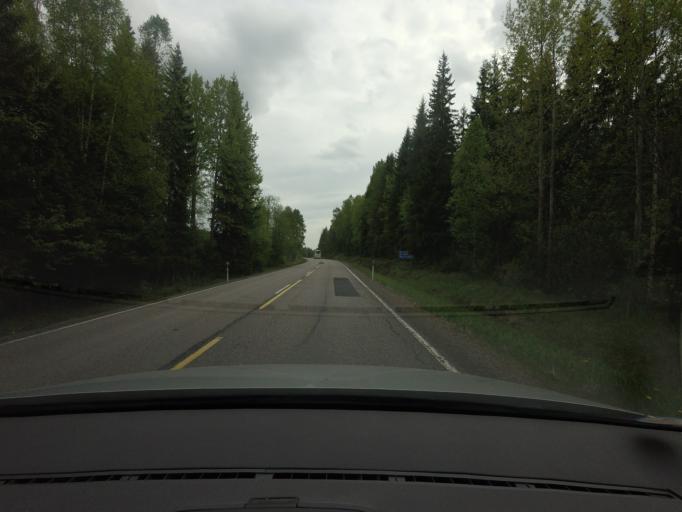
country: FI
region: South Karelia
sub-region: Lappeenranta
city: Taavetti
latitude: 60.8113
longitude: 27.3883
